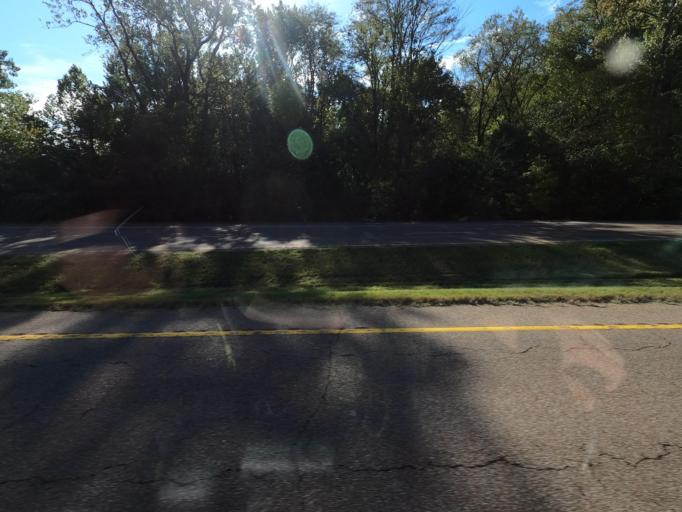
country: US
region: Tennessee
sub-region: Tipton County
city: Brighton
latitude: 35.4919
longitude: -89.7269
